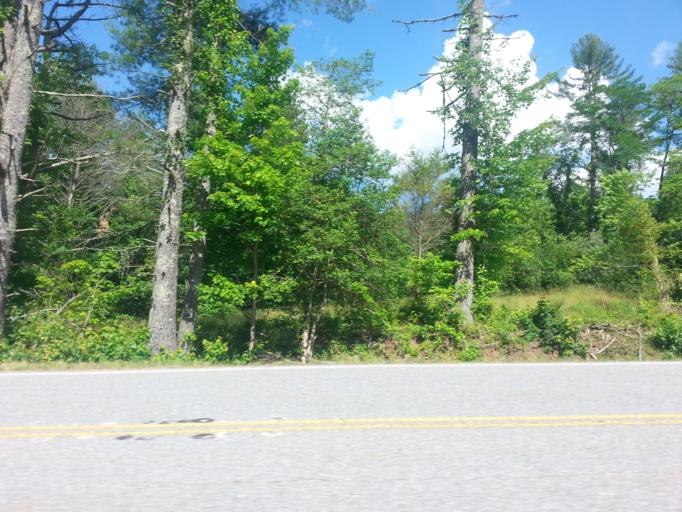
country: US
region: Georgia
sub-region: Towns County
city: Hiawassee
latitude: 34.8557
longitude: -83.7225
